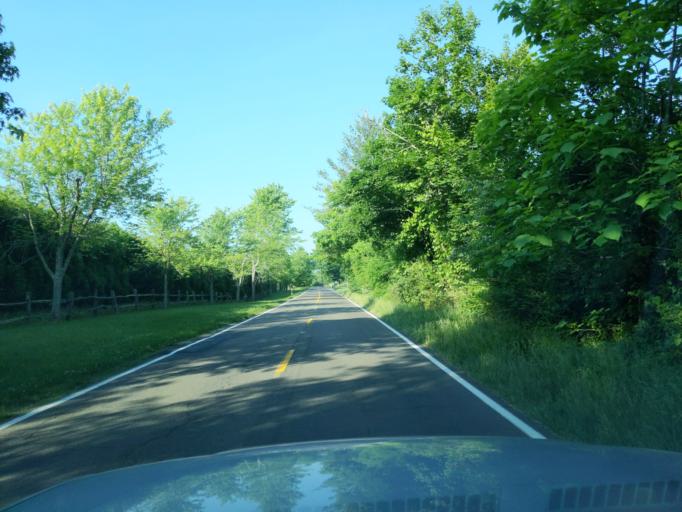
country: US
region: North Carolina
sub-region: Henderson County
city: Hoopers Creek
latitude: 35.4662
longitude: -82.4624
